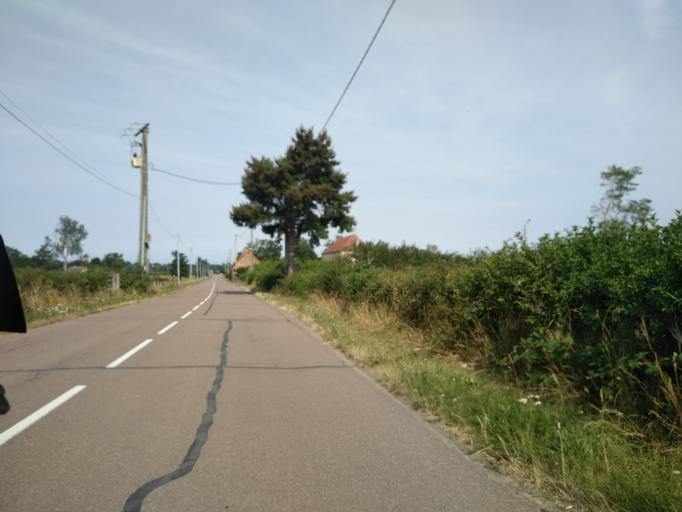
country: FR
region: Bourgogne
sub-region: Departement de Saone-et-Loire
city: Saint-Yan
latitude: 46.3553
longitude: 4.0045
